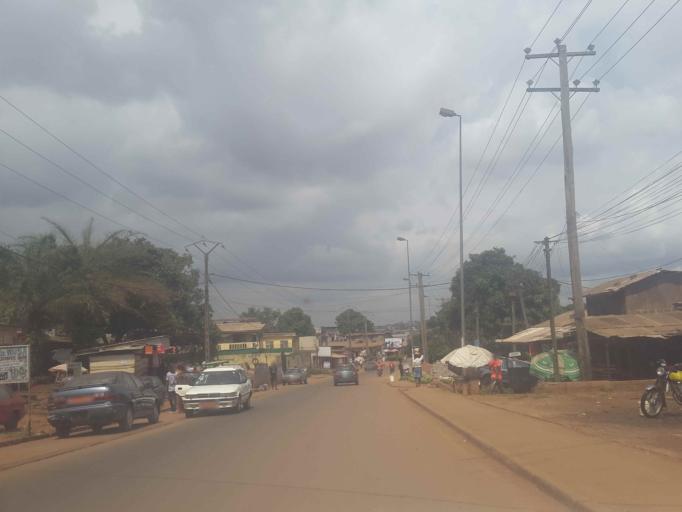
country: CM
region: Centre
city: Yaounde
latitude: 3.8737
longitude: 11.4780
